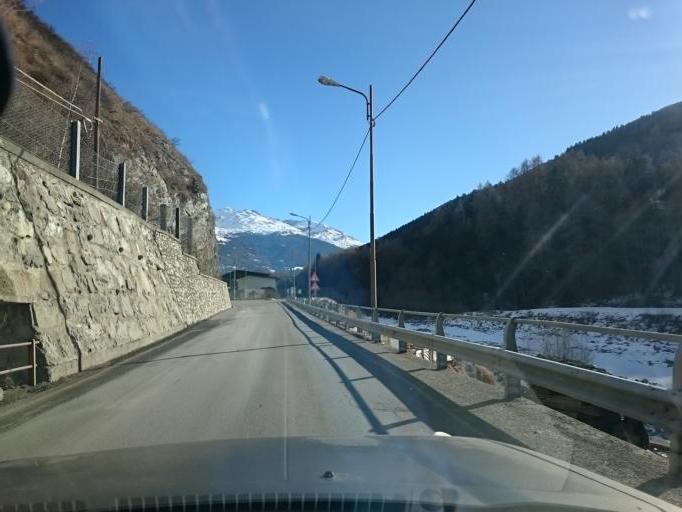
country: IT
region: Lombardy
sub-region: Provincia di Sondrio
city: Bormio
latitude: 46.4664
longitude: 10.3844
